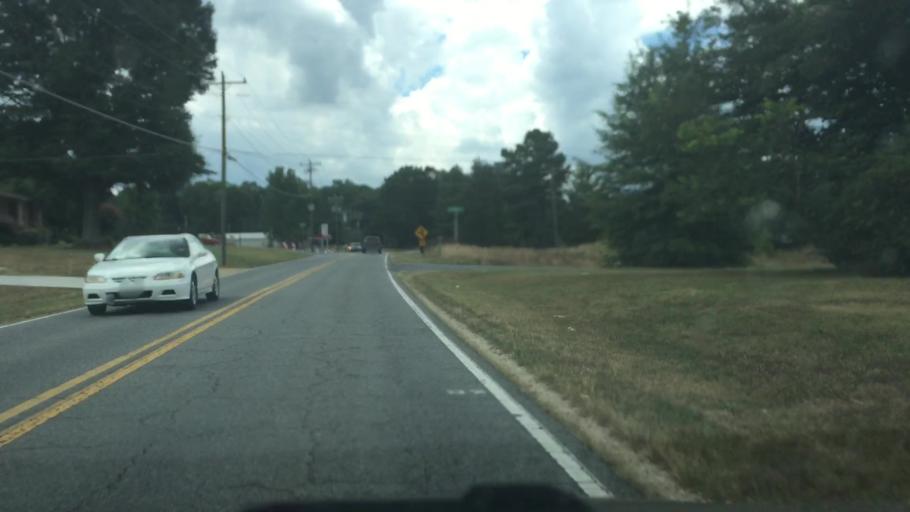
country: US
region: North Carolina
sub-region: Rowan County
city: Enochville
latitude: 35.5186
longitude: -80.6699
